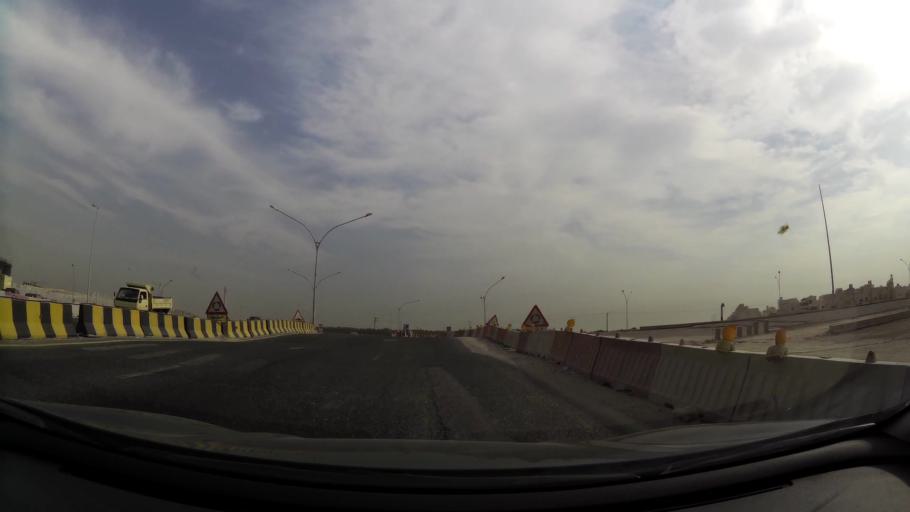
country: KW
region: Muhafazat al Jahra'
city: Al Jahra'
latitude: 29.3353
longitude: 47.7985
